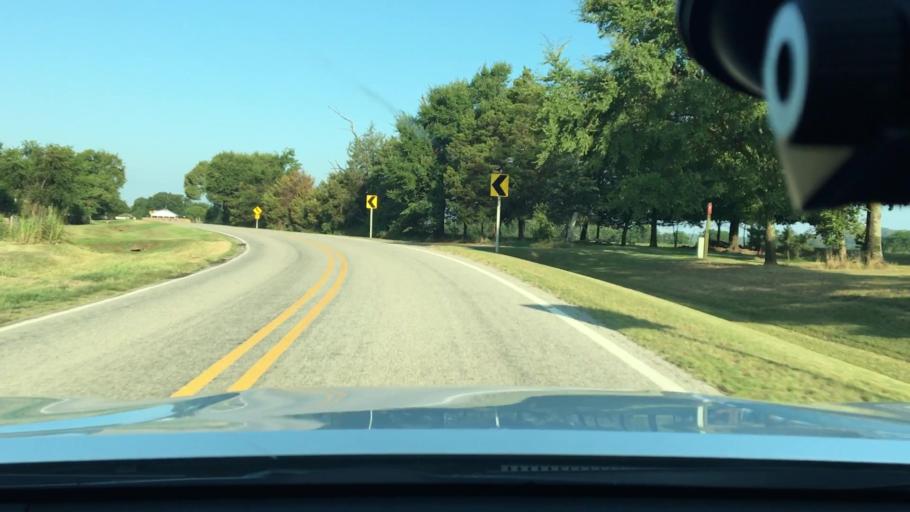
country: US
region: Arkansas
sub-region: Johnson County
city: Coal Hill
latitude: 35.3406
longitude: -93.6002
